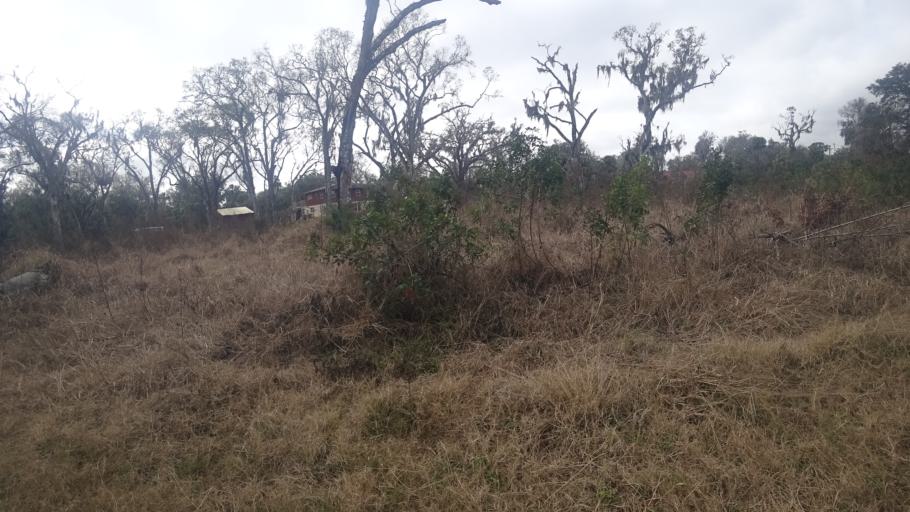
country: US
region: Florida
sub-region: Manatee County
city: Ellenton
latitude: 27.5804
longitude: -82.5020
